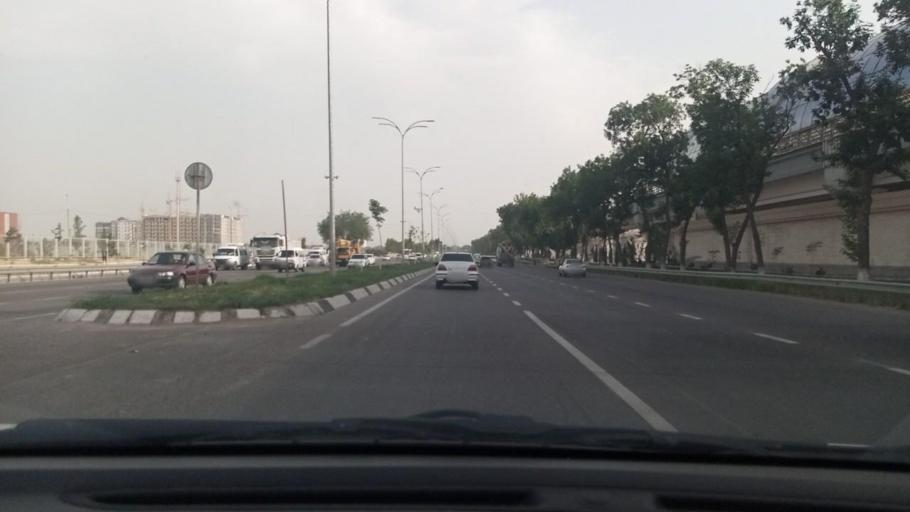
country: UZ
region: Toshkent Shahri
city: Bektemir
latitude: 41.2823
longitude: 69.3607
